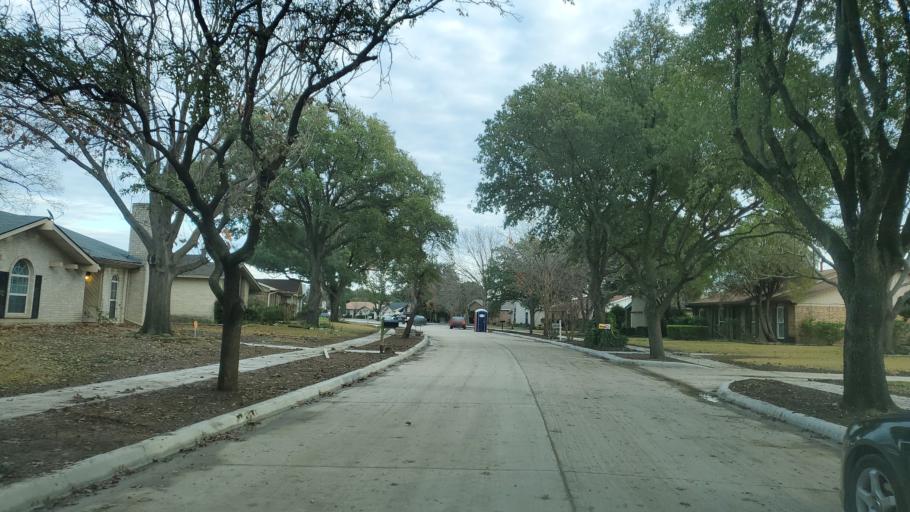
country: US
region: Texas
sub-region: Dallas County
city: Carrollton
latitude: 33.0033
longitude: -96.8795
